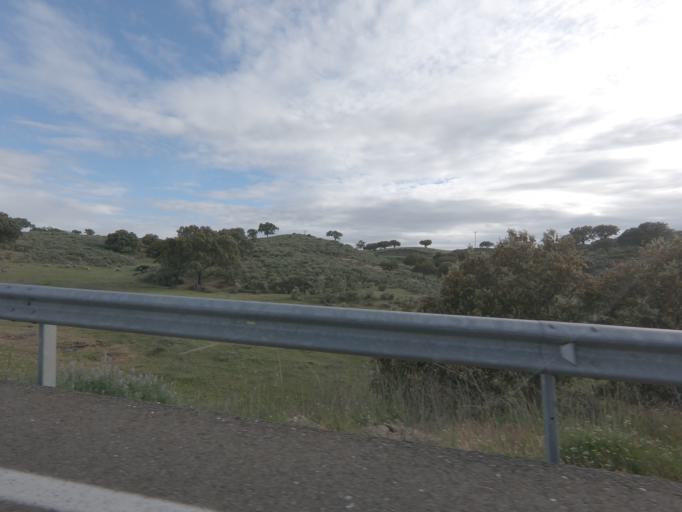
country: ES
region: Extremadura
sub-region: Provincia de Caceres
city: Huelaga
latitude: 40.0314
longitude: -6.6138
